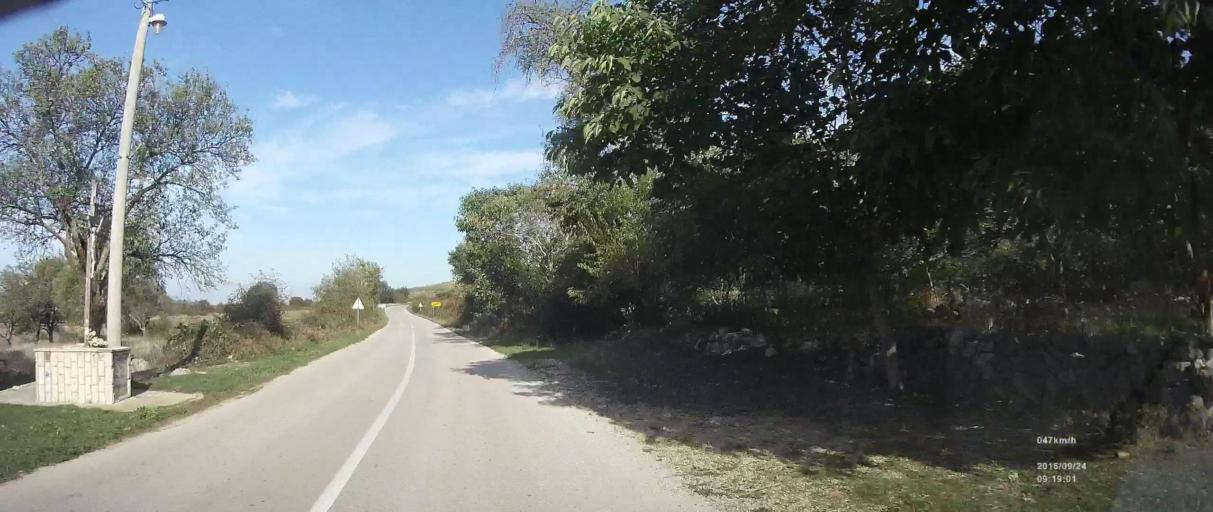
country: HR
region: Zadarska
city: Polaca
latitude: 44.0597
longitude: 15.5077
